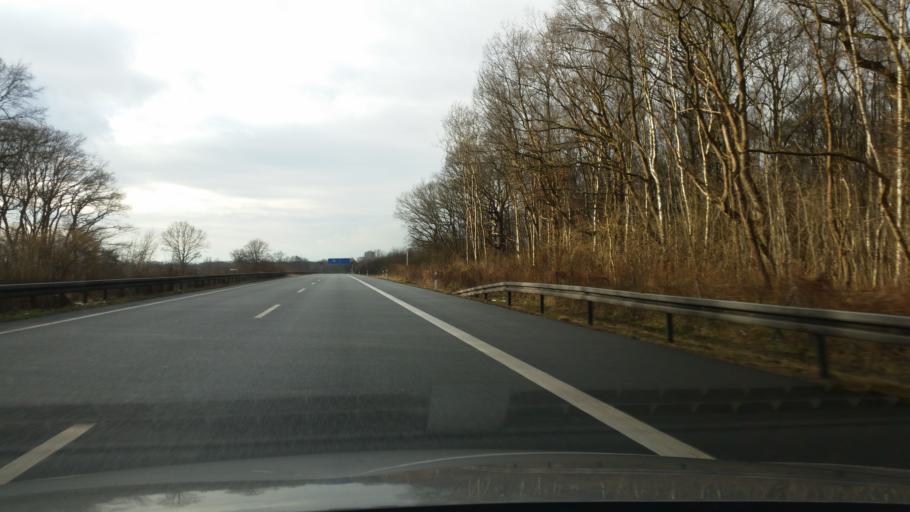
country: DE
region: Lower Saxony
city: Laatzen
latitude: 52.3053
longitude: 9.8461
